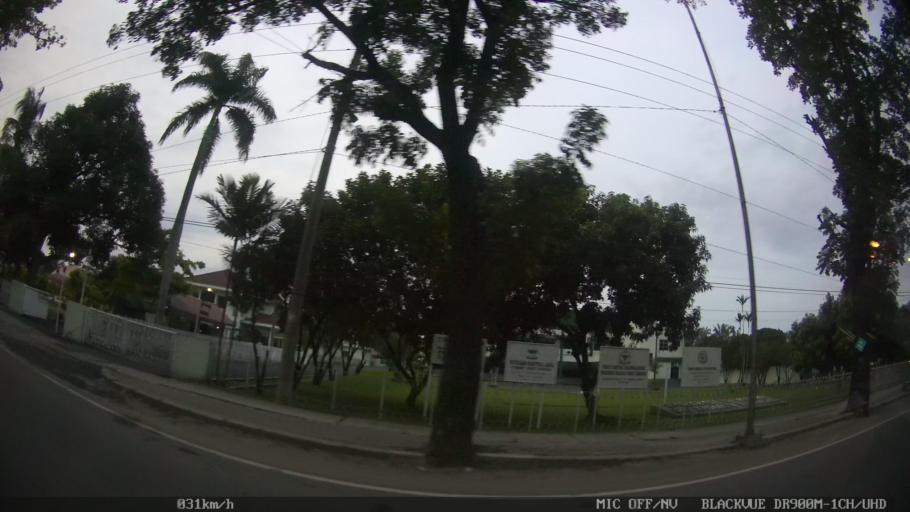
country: ID
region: North Sumatra
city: Sunggal
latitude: 3.5941
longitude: 98.6189
